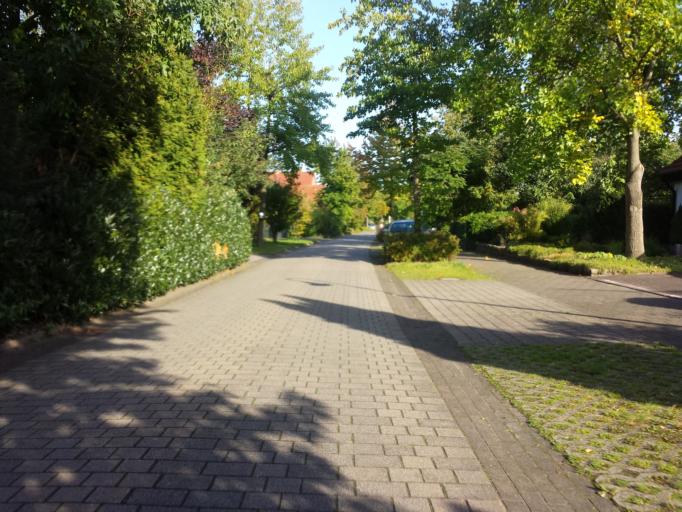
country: DE
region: North Rhine-Westphalia
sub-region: Regierungsbezirk Detmold
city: Langenberg
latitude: 51.7672
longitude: 8.3172
